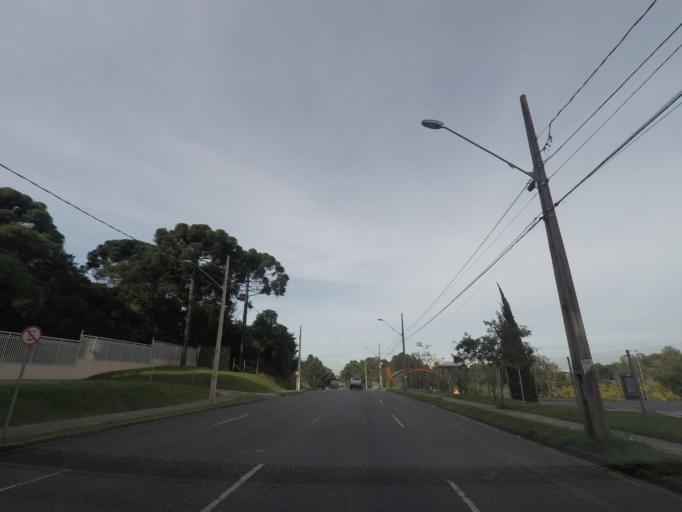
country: BR
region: Parana
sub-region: Curitiba
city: Curitiba
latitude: -25.4467
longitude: -49.3557
